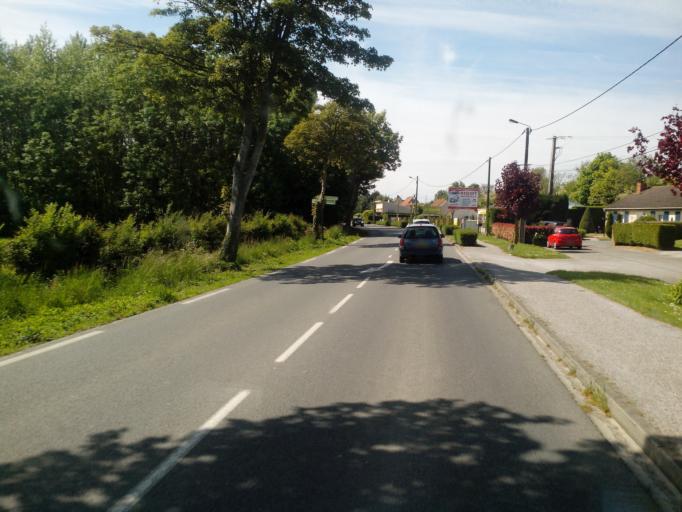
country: FR
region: Nord-Pas-de-Calais
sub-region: Departement du Pas-de-Calais
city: Saint-Josse
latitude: 50.4976
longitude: 1.6986
